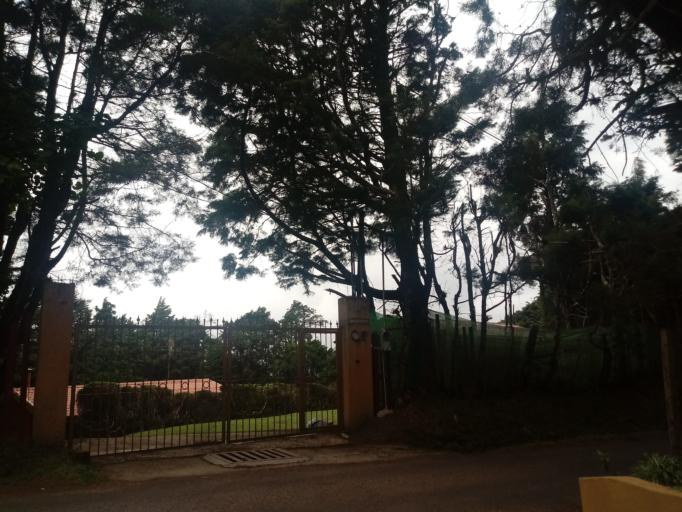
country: CR
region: Heredia
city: Angeles
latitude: 10.0405
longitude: -84.0415
